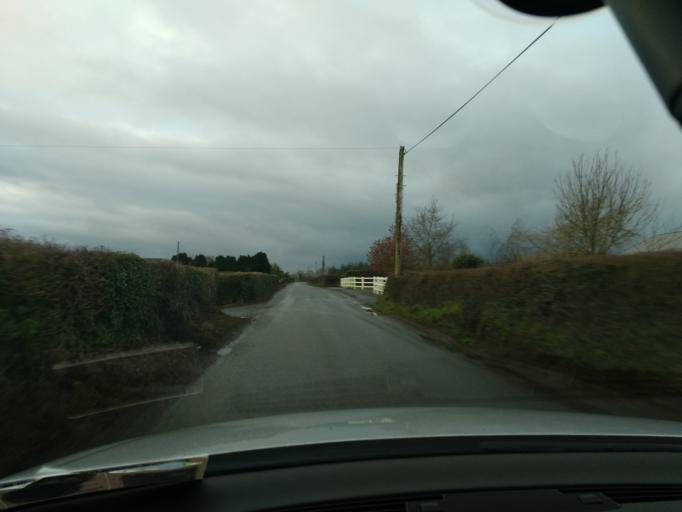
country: IE
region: Munster
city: Thurles
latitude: 52.6362
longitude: -7.8415
